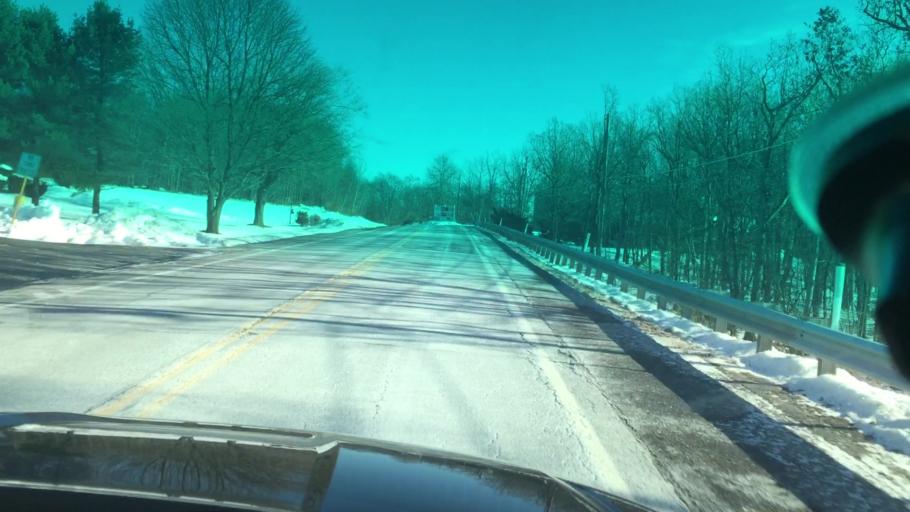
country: US
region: Pennsylvania
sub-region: Luzerne County
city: Freeland
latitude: 41.0158
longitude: -75.9151
